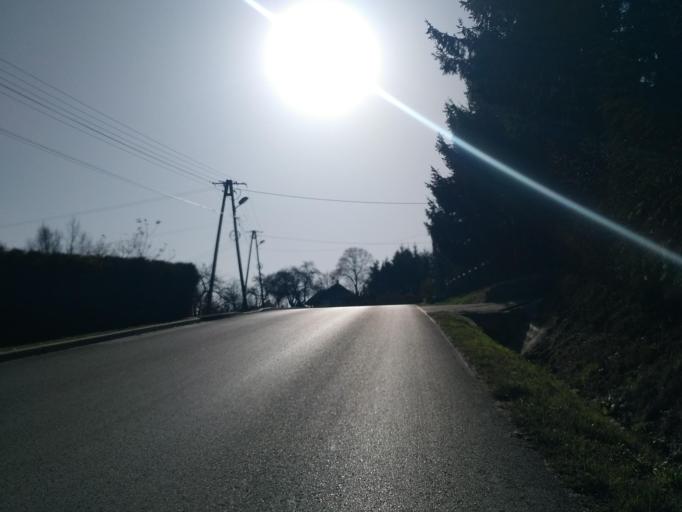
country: PL
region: Subcarpathian Voivodeship
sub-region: Powiat brzozowski
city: Nozdrzec
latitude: 49.8179
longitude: 22.1660
